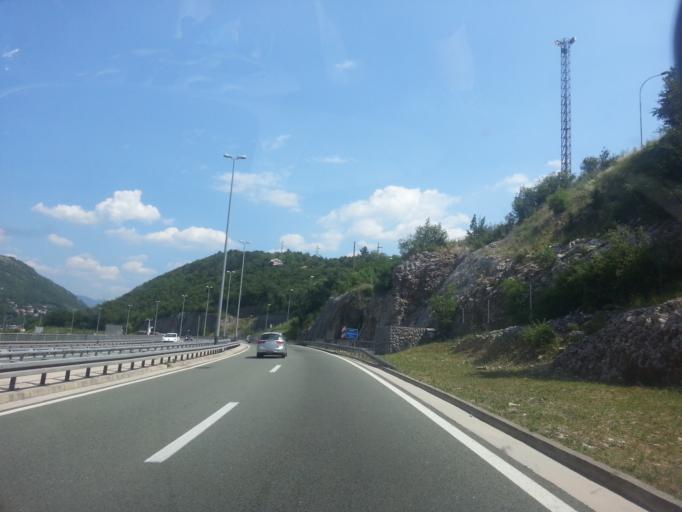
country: HR
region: Primorsko-Goranska
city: Cavle
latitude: 45.3283
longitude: 14.4762
